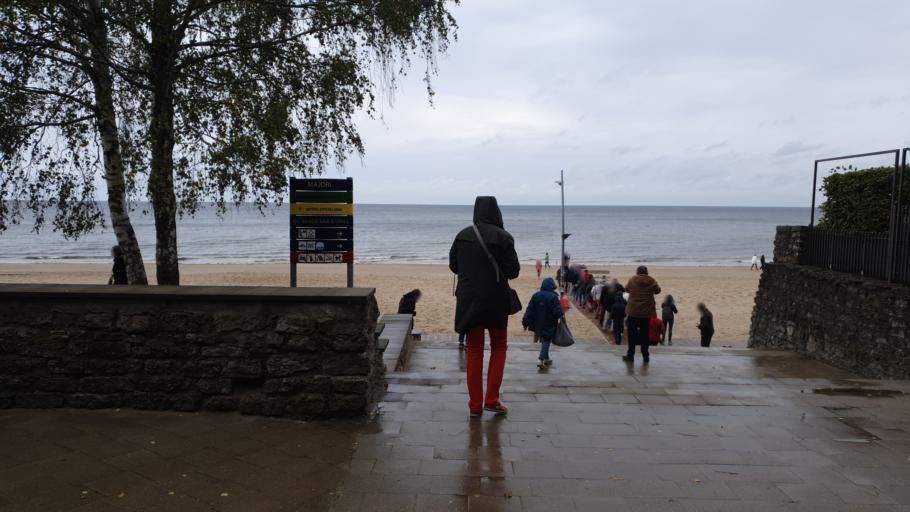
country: LV
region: Jurmala
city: Jurmala
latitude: 56.9763
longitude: 23.7979
